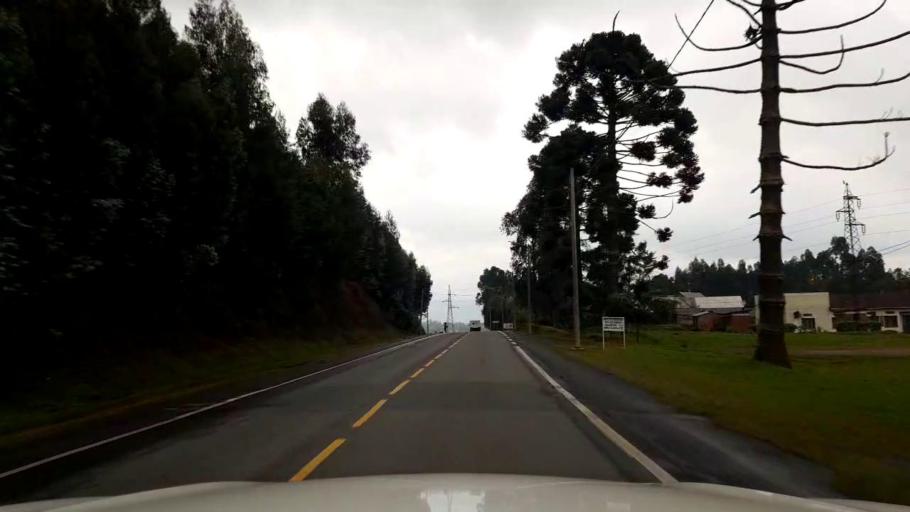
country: RW
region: Northern Province
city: Musanze
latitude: -1.5381
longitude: 29.5614
